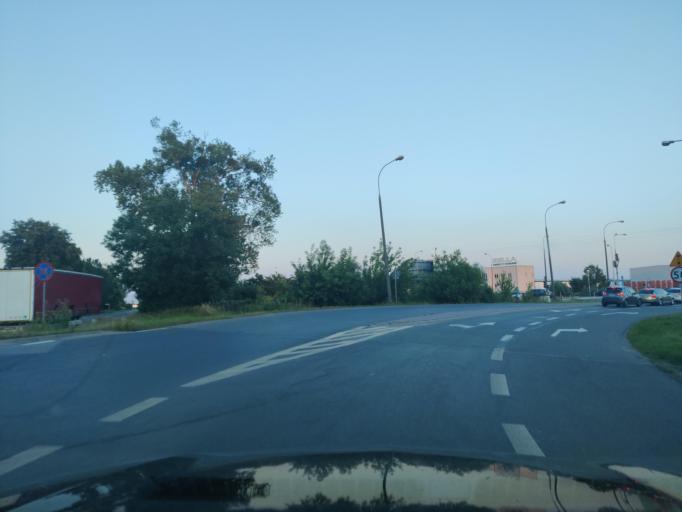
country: PL
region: Masovian Voivodeship
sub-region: Powiat nowodworski
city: Nowy Dwor Mazowiecki
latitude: 52.3885
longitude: 20.7382
